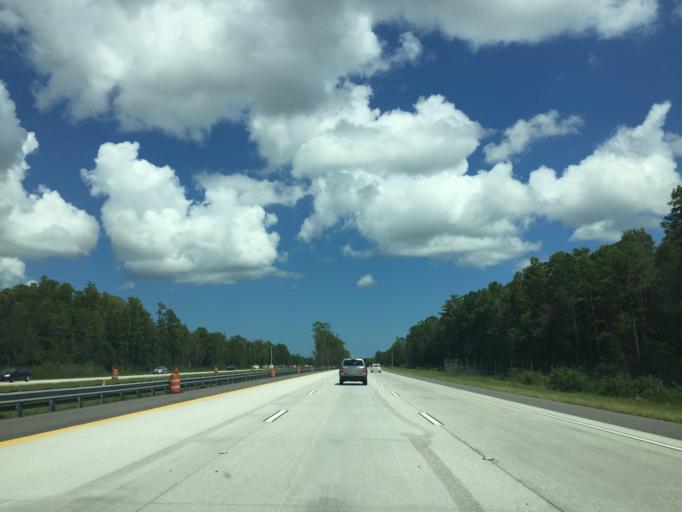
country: US
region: Florida
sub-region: Volusia County
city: Samsula-Spruce Creek
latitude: 29.0877
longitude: -81.1652
